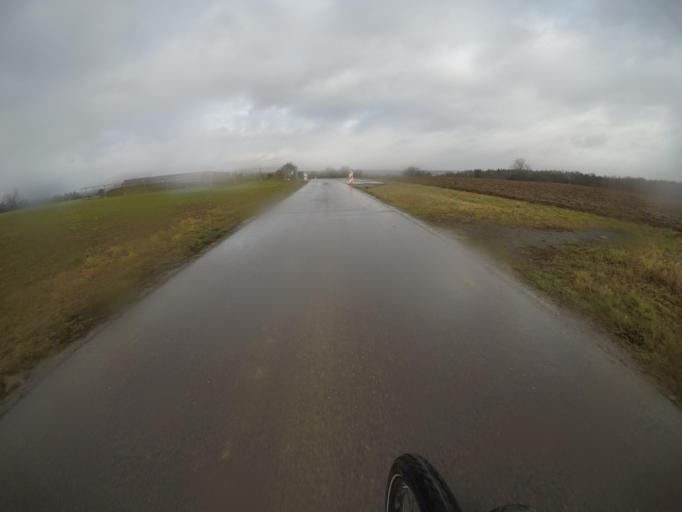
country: DE
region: Baden-Wuerttemberg
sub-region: Regierungsbezirk Stuttgart
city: Eberdingen
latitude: 48.8990
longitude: 8.9977
